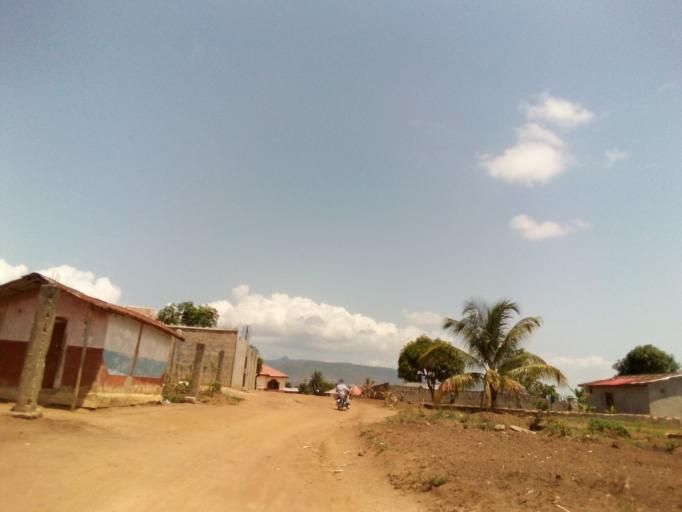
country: SL
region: Western Area
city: Waterloo
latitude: 8.3408
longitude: -13.0310
